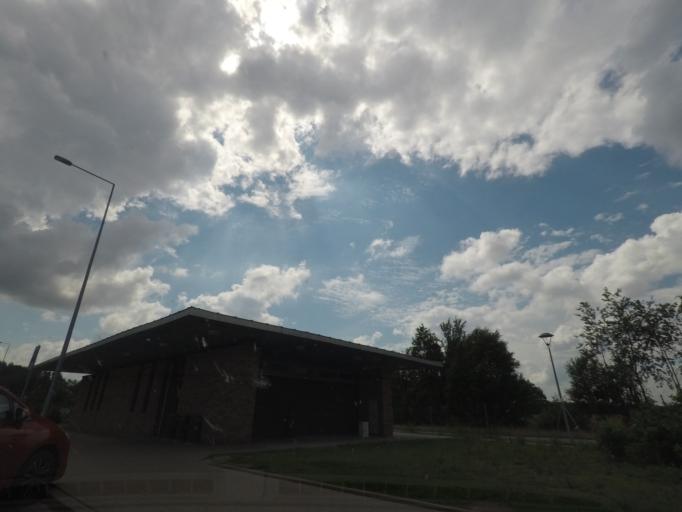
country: PL
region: Lodz Voivodeship
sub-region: Powiat leczycki
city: Piatek
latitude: 52.0055
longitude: 19.5428
